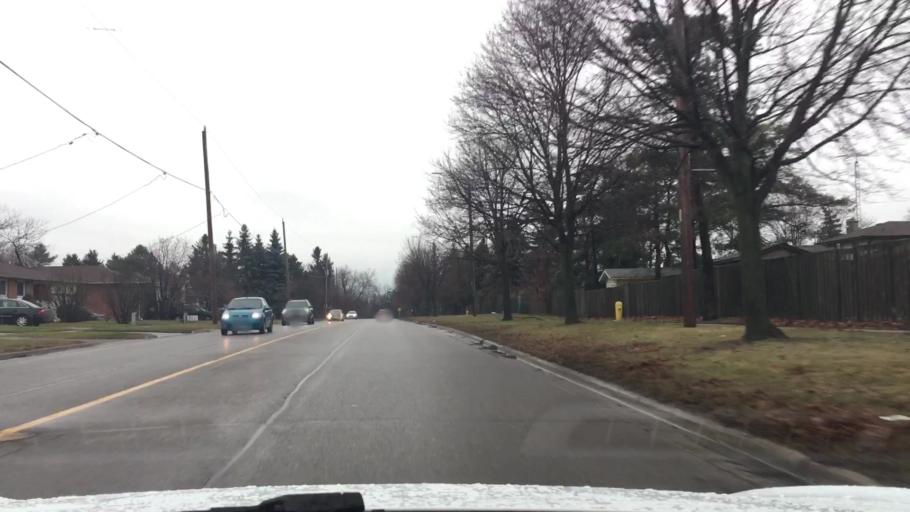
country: CA
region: Ontario
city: Oshawa
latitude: 43.9011
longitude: -78.8110
